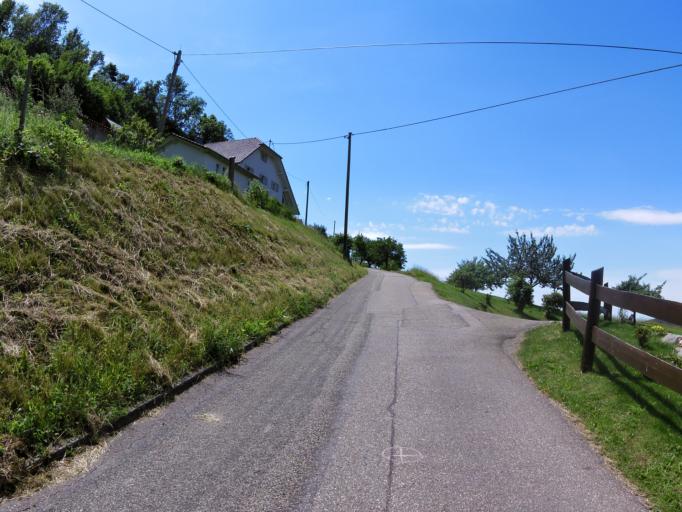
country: DE
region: Baden-Wuerttemberg
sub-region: Freiburg Region
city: Seelbach
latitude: 48.3337
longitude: 7.9789
